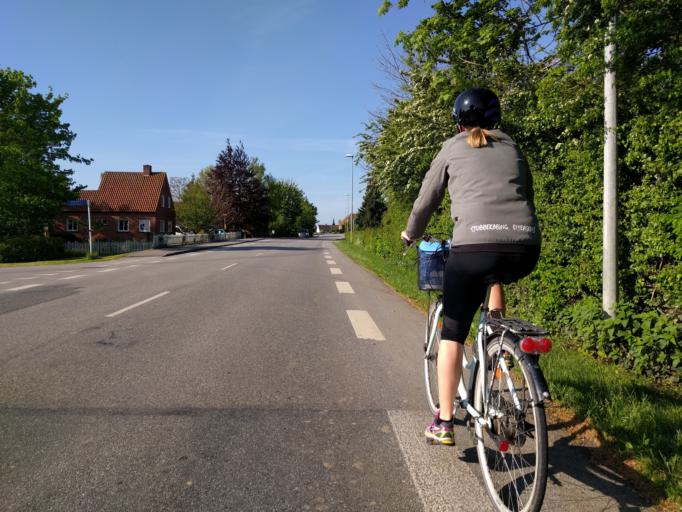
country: DK
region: Zealand
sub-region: Guldborgsund Kommune
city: Stubbekobing
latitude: 54.8659
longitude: 12.0210
